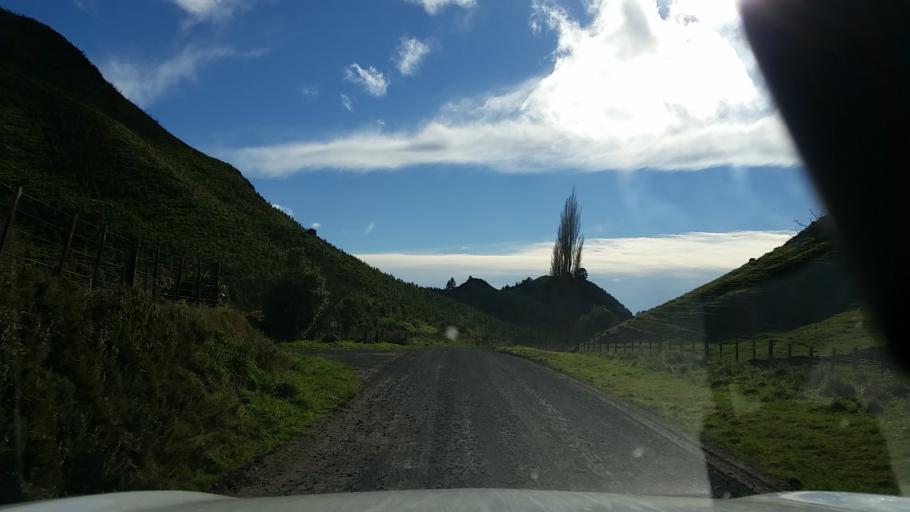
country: NZ
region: Bay of Plenty
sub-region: Rotorua District
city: Rotorua
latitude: -38.3647
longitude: 176.2079
